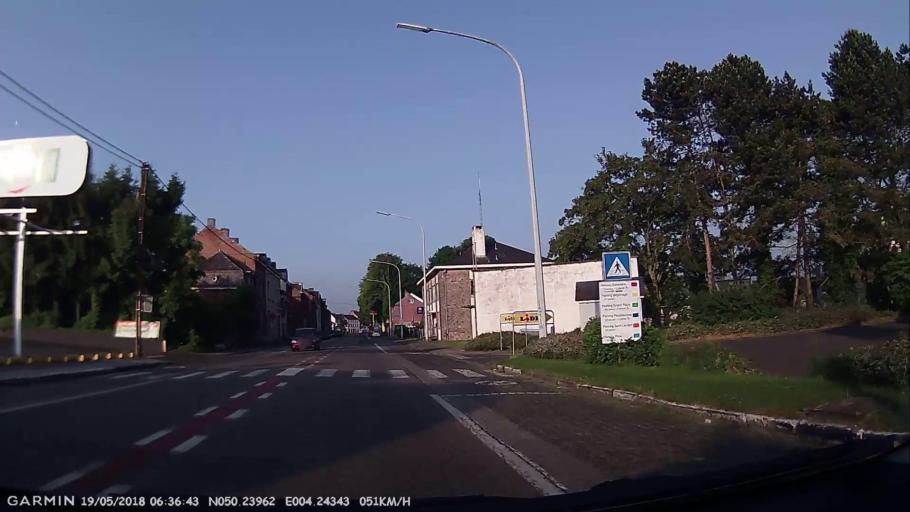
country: BE
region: Wallonia
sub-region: Province du Hainaut
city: Beaumont
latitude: 50.2395
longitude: 4.2433
